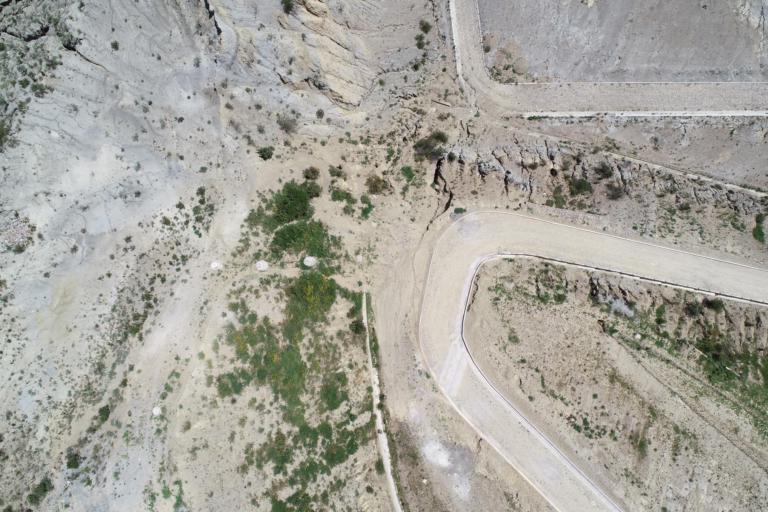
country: BO
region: La Paz
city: La Paz
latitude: -16.5237
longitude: -68.0461
